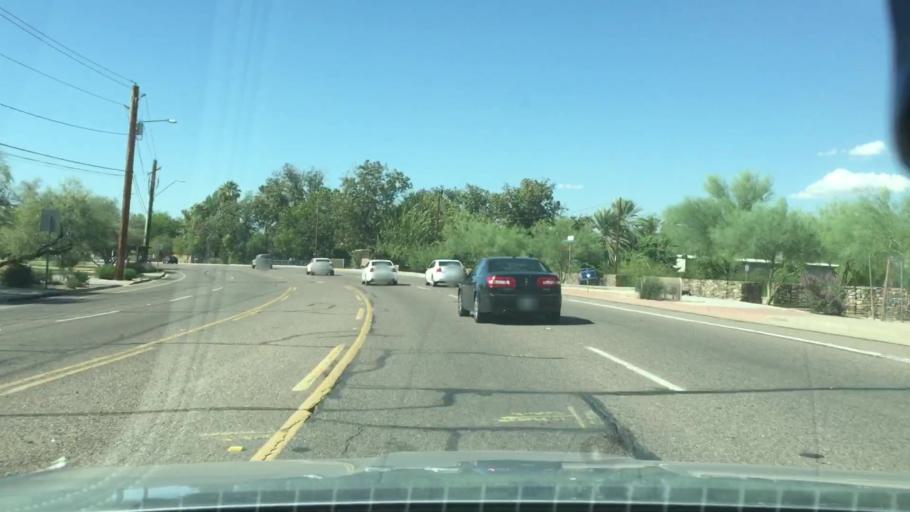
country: US
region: Arizona
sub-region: Maricopa County
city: Guadalupe
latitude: 33.3937
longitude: -112.0158
